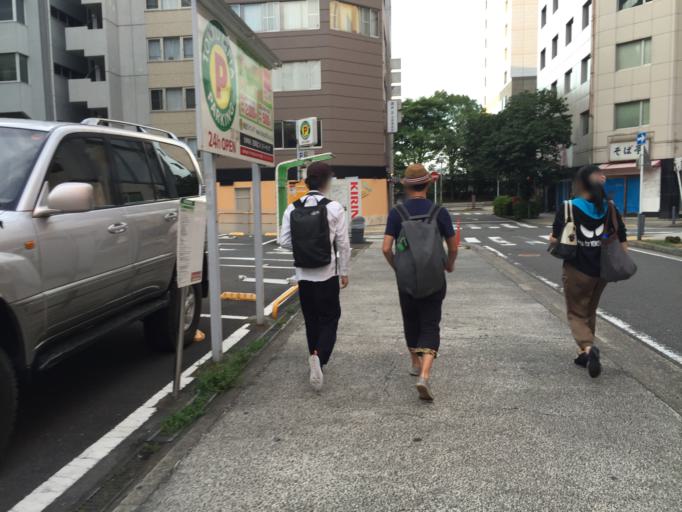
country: JP
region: Kanagawa
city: Yokohama
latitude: 35.4492
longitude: 139.6399
